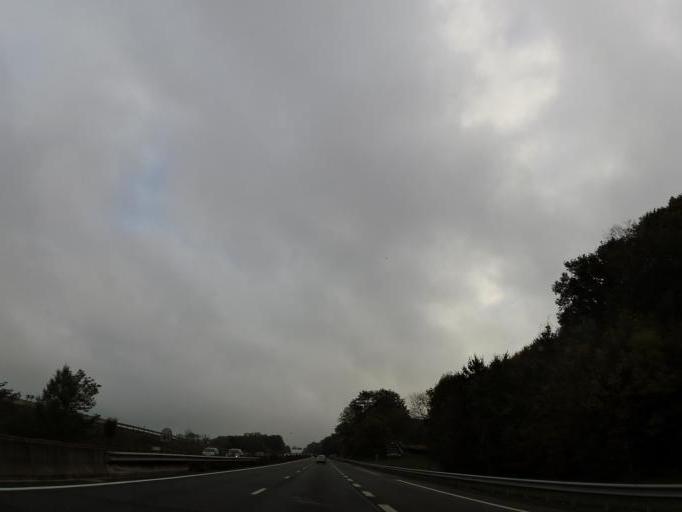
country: FR
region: Ile-de-France
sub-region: Departement de Seine-et-Marne
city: Bouleurs
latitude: 48.8875
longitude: 2.8984
